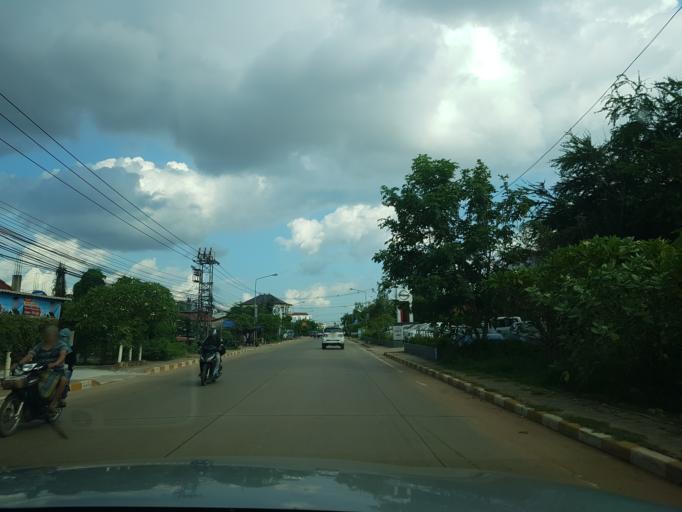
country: TH
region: Nong Khai
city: Si Chiang Mai
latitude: 17.9756
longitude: 102.5455
